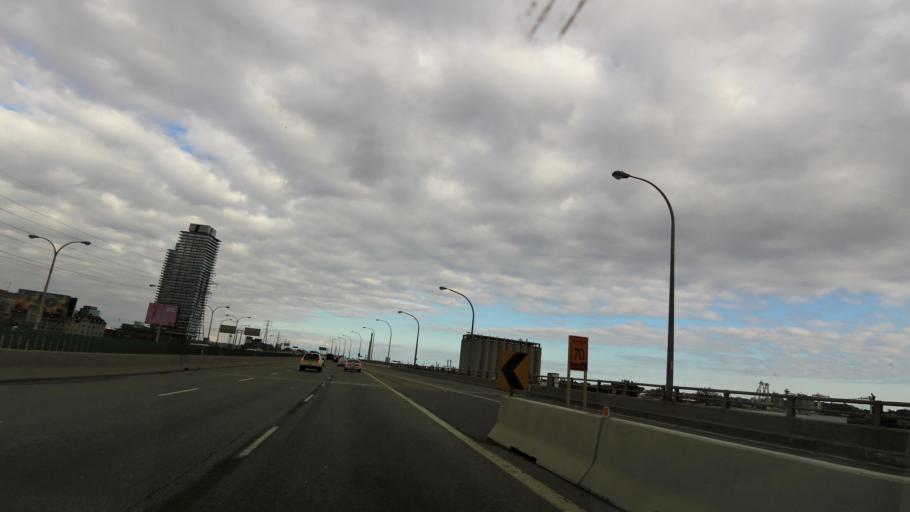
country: CA
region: Ontario
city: Toronto
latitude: 43.6471
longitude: -79.3634
